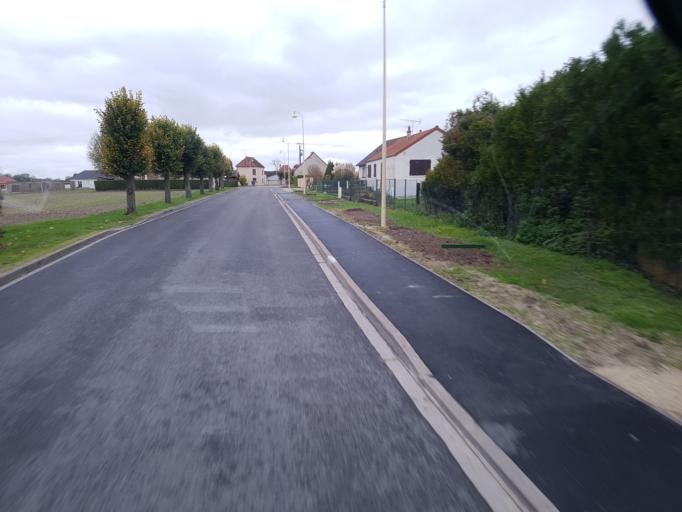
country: FR
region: Champagne-Ardenne
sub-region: Departement de la Marne
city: Saint-Just-Sauvage
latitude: 48.5826
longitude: 3.8509
